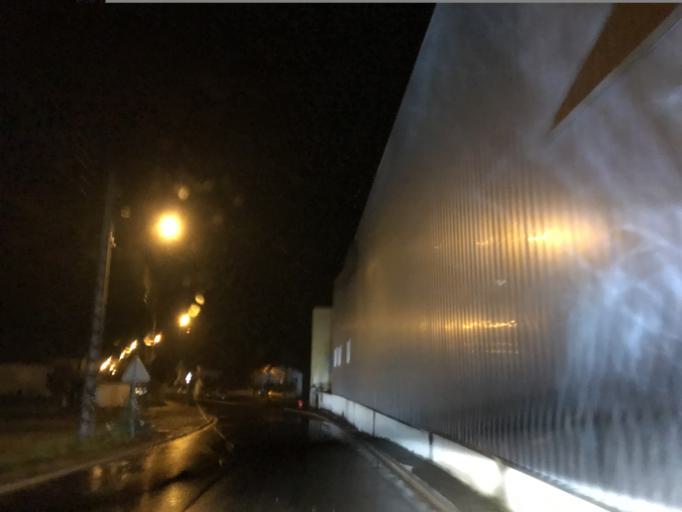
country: FR
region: Auvergne
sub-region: Departement du Puy-de-Dome
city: Celles-sur-Durolle
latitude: 45.8854
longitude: 3.6412
